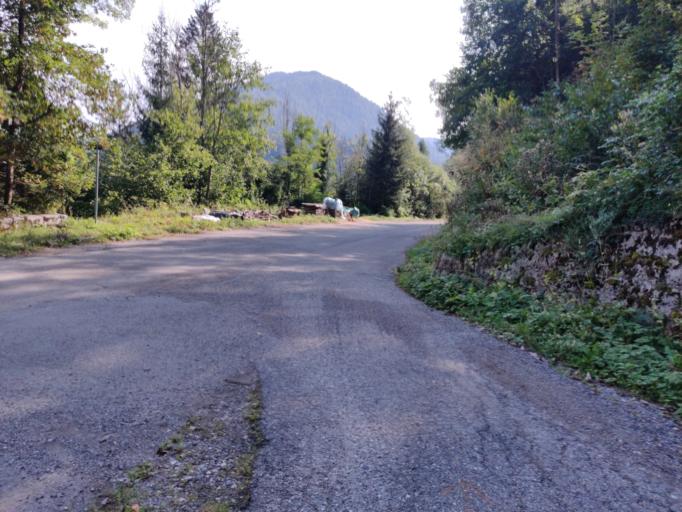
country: IT
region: Friuli Venezia Giulia
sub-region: Provincia di Udine
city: Tarvisio
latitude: 46.5192
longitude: 13.6109
